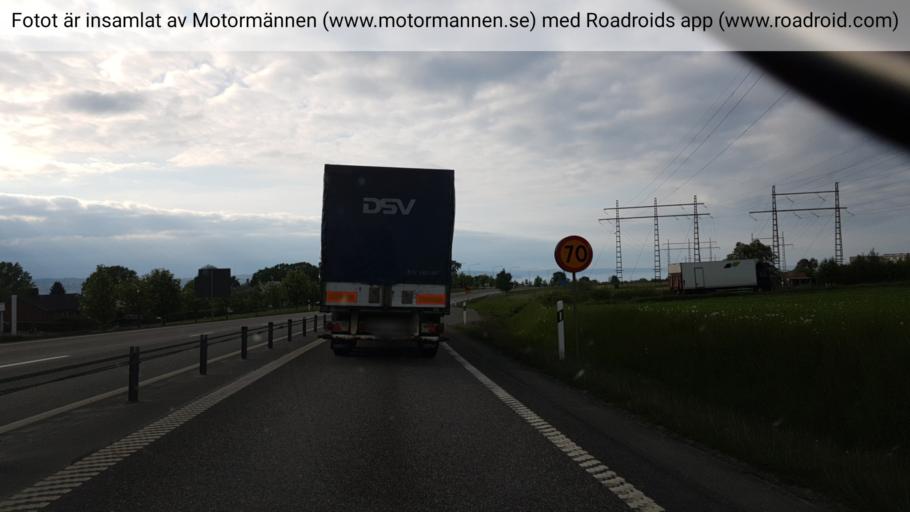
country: SE
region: Joenkoeping
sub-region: Jonkopings Kommun
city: Jonkoping
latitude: 57.7692
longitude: 14.2218
